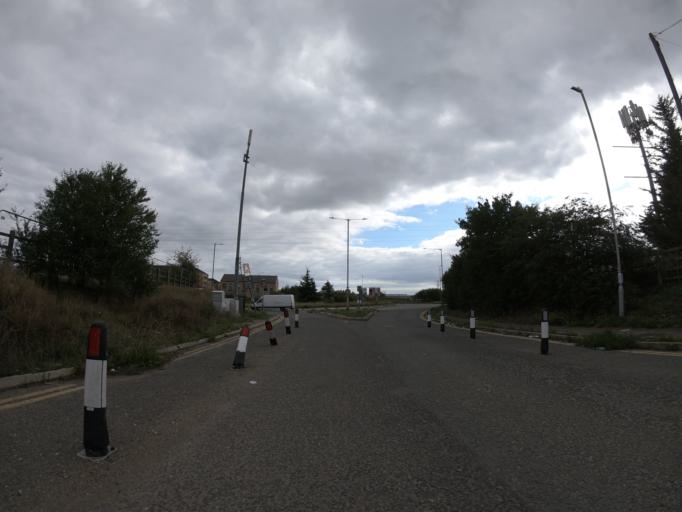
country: GB
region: England
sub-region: Kent
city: Dartford
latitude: 51.4597
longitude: 0.2199
